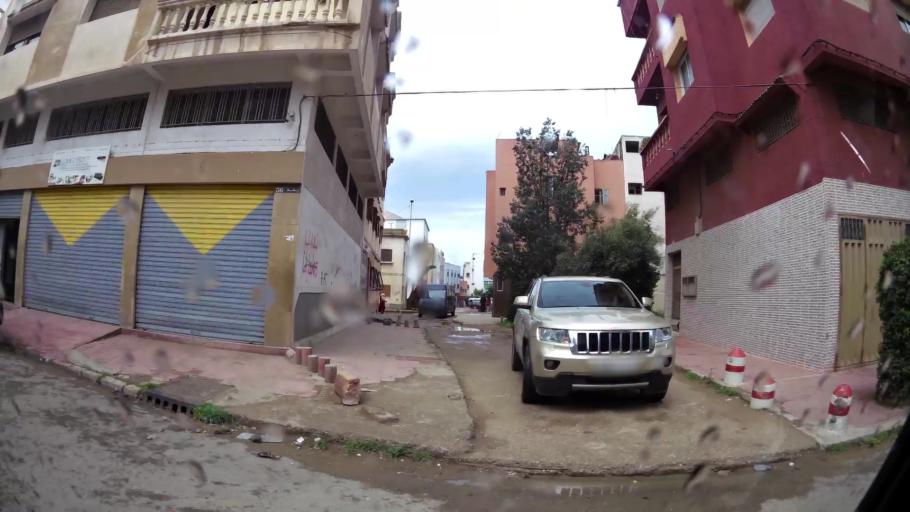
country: MA
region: Grand Casablanca
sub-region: Casablanca
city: Casablanca
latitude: 33.5502
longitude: -7.6874
